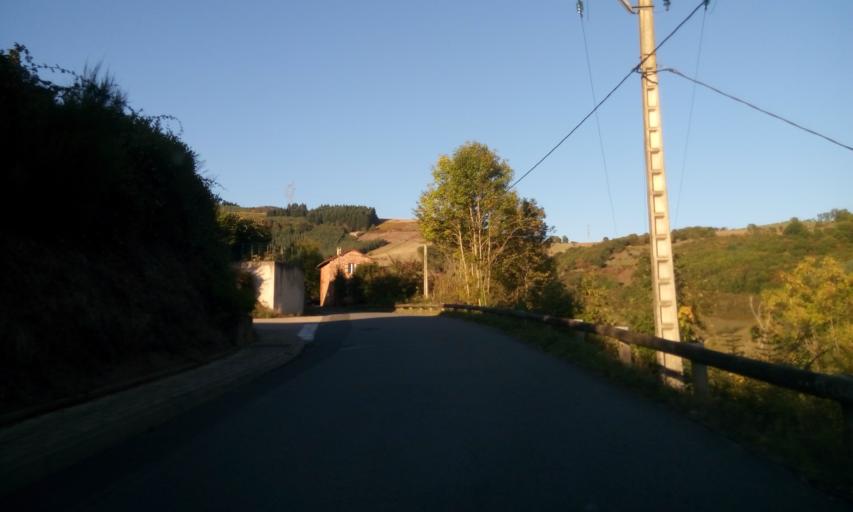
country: FR
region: Rhone-Alpes
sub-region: Departement du Rhone
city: Tarare
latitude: 45.9465
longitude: 4.4345
